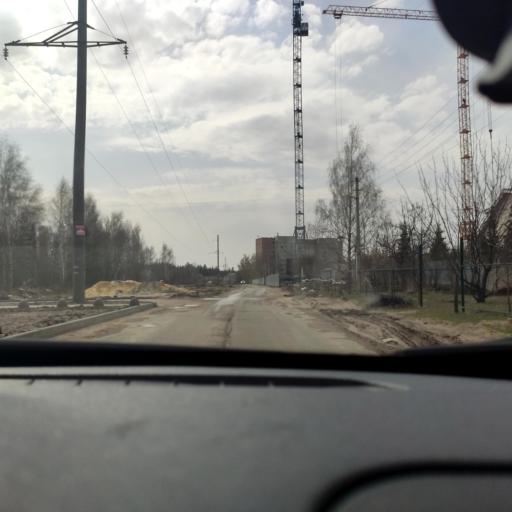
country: RU
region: Voronezj
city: Podgornoye
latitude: 51.7596
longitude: 39.1756
